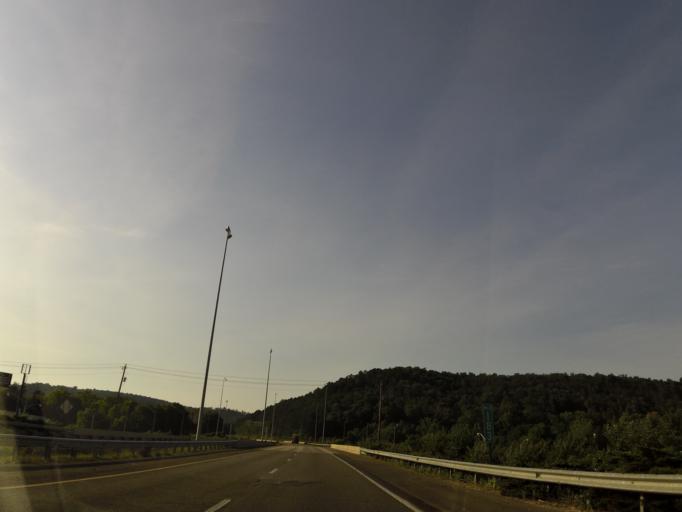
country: US
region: Alabama
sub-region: Etowah County
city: Attalla
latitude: 34.0182
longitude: -86.0745
